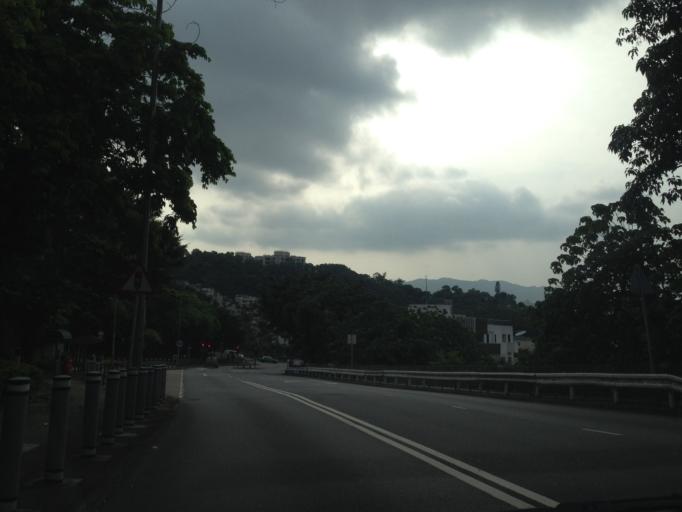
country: HK
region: Tai Po
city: Tai Po
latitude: 22.4424
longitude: 114.1787
